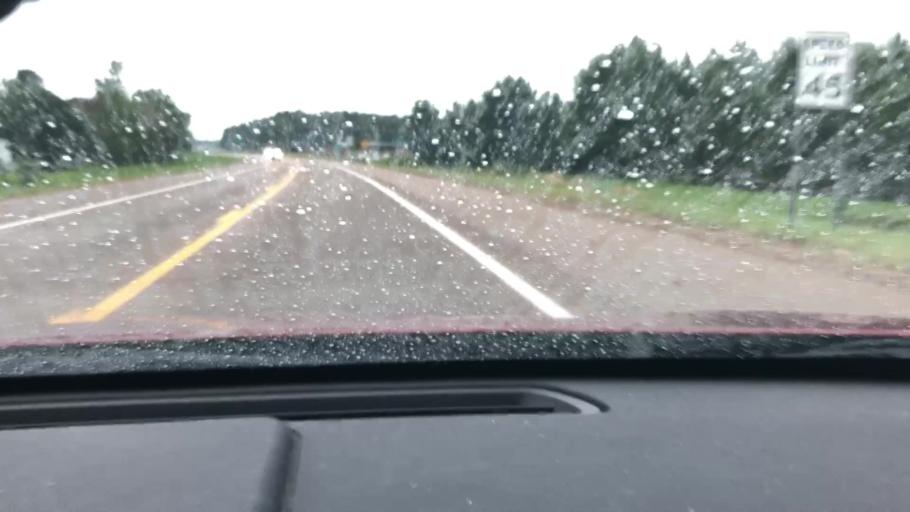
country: US
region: Arkansas
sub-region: Columbia County
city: Magnolia
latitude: 33.2964
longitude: -93.2557
